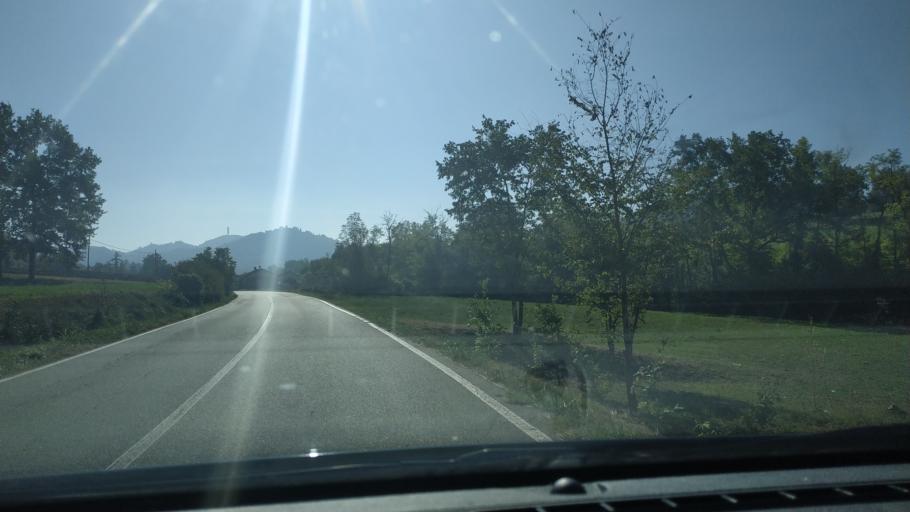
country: IT
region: Piedmont
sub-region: Provincia di Alessandria
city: Murisengo
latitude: 45.0896
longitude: 8.1441
